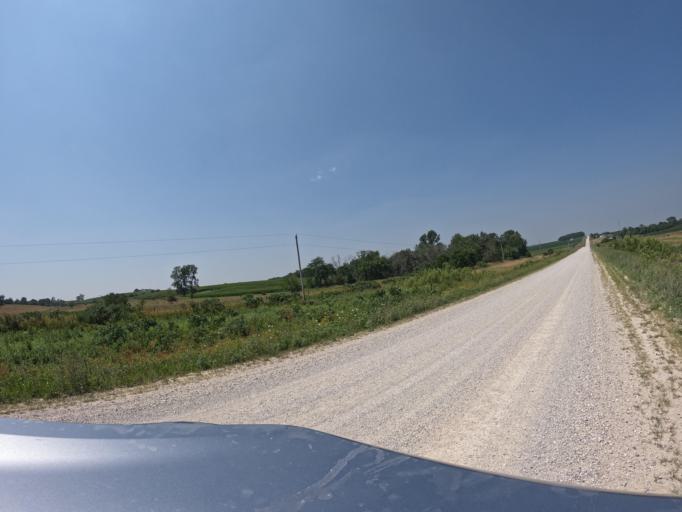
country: US
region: Iowa
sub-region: Keokuk County
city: Sigourney
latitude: 41.3487
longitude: -92.2389
